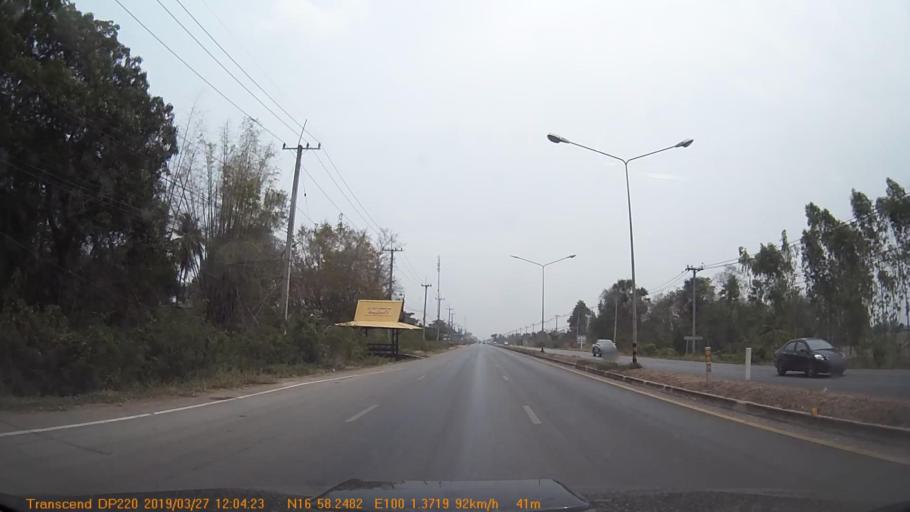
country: TH
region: Sukhothai
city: Kong Krailat
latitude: 16.9708
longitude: 100.0233
